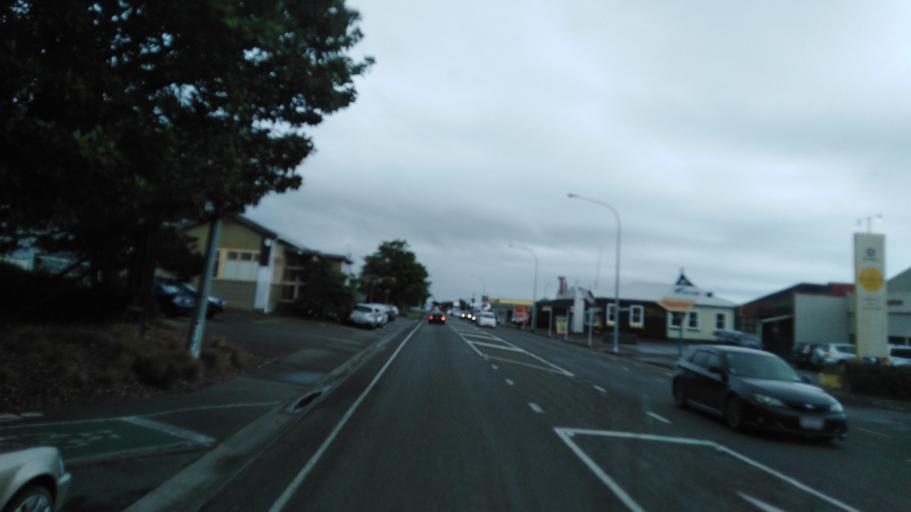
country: NZ
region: Manawatu-Wanganui
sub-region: Horowhenua District
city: Levin
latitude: -40.6307
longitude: 175.2780
